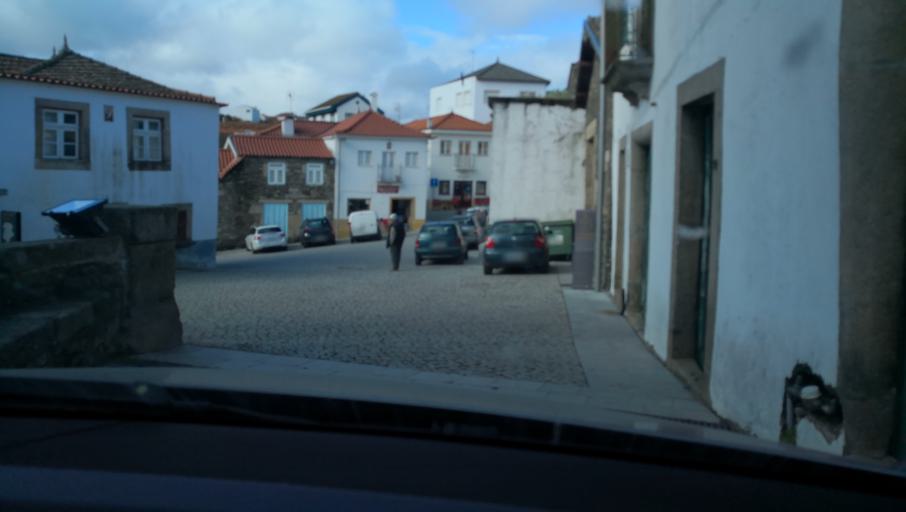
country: PT
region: Vila Real
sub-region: Sabrosa
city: Vilela
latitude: 41.2178
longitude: -7.5668
